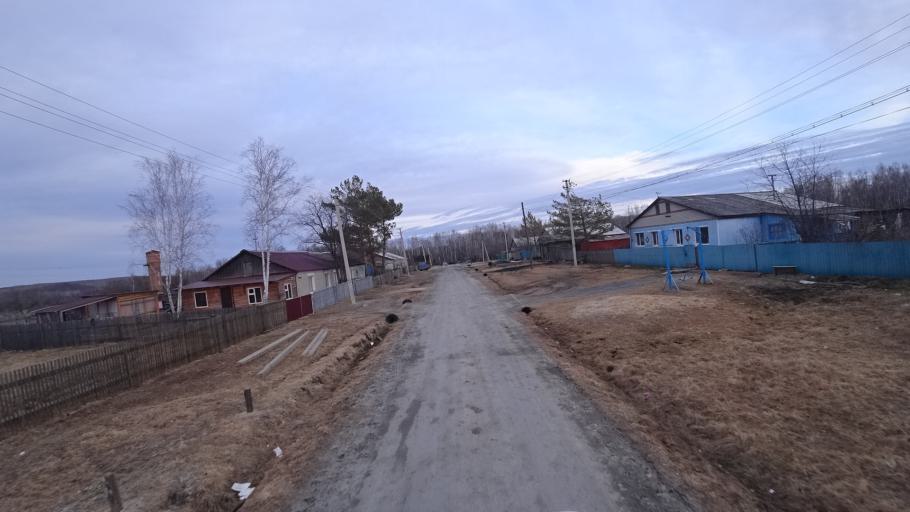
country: RU
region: Amur
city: Bureya
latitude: 50.0155
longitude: 129.7684
